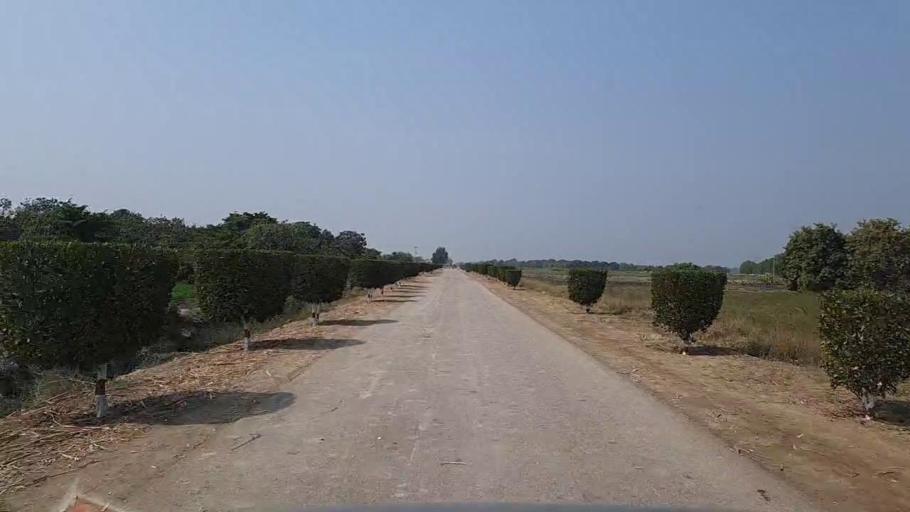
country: PK
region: Sindh
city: Mirwah Gorchani
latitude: 25.3358
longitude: 68.9973
